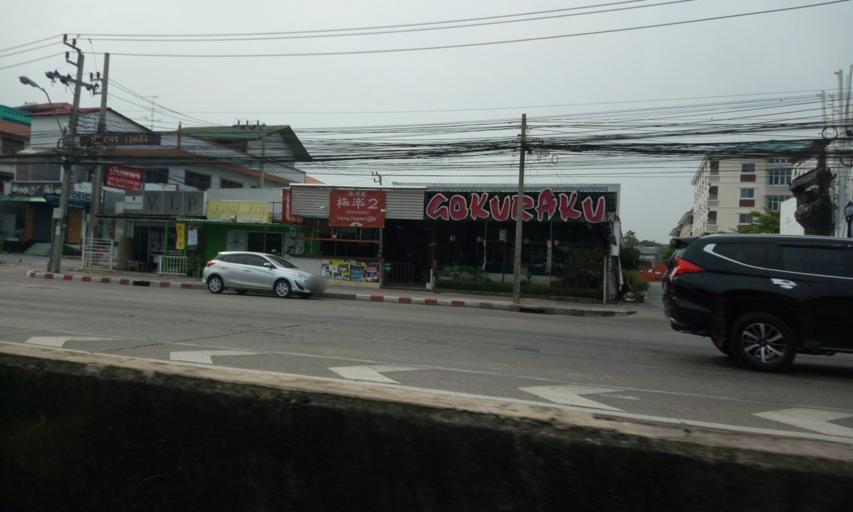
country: TH
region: Bangkok
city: Lat Krabang
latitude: 13.7217
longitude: 100.7736
